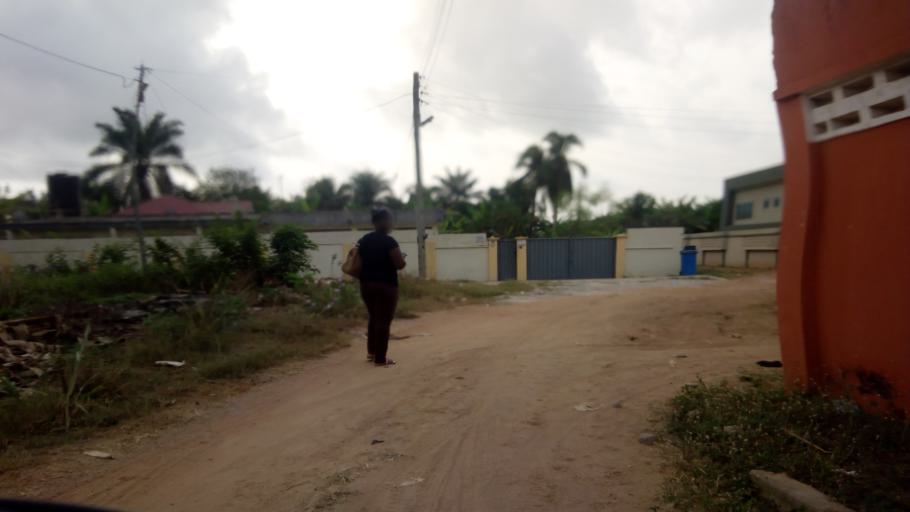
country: GH
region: Central
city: Cape Coast
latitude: 5.1249
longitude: -1.2777
